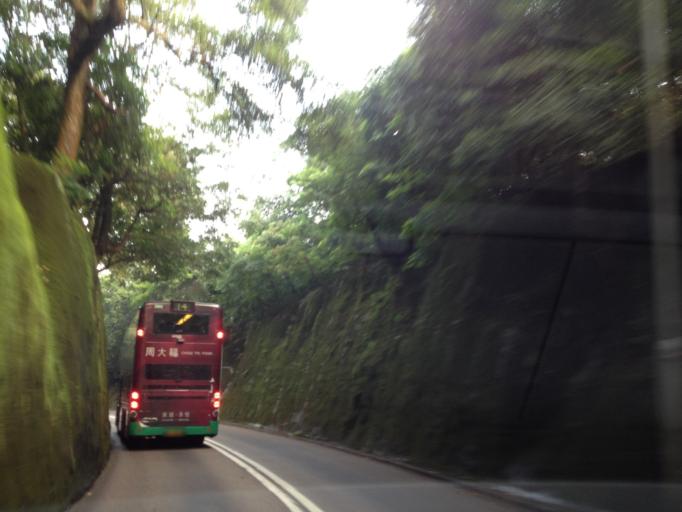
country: HK
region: Wanchai
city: Wan Chai
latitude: 22.2624
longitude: 114.2272
